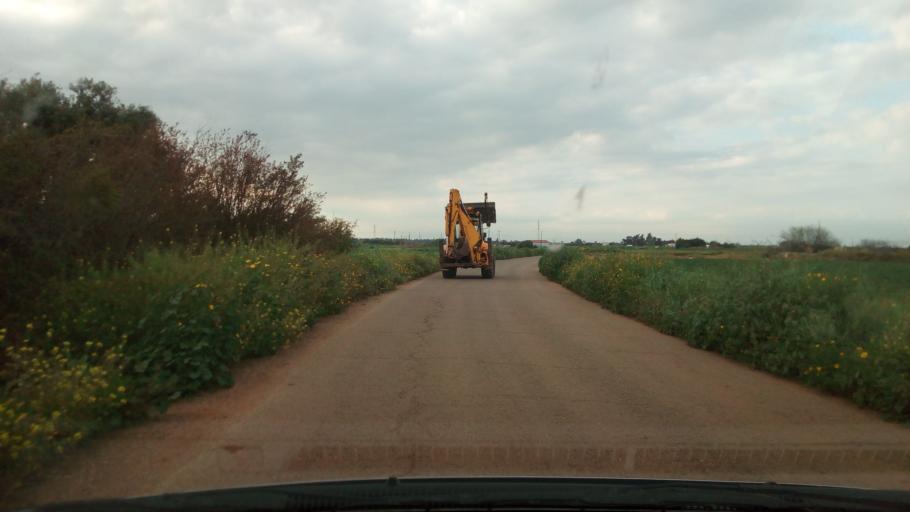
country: CY
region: Ammochostos
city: Avgorou
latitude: 34.9897
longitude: 33.8295
